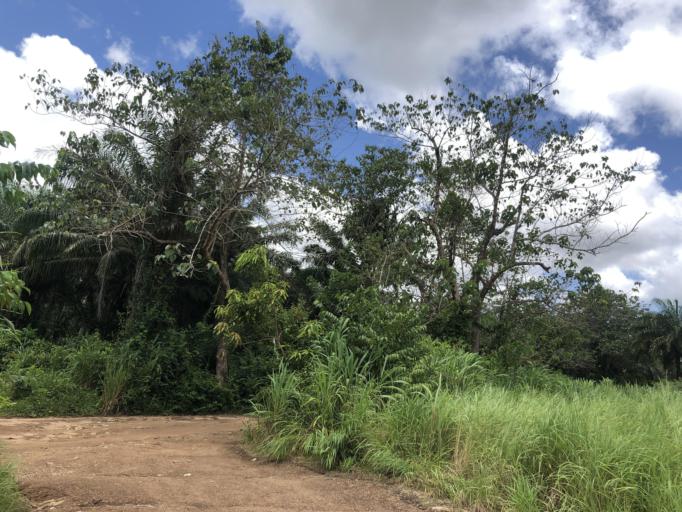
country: SL
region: Northern Province
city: Makeni
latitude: 8.8558
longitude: -12.0625
